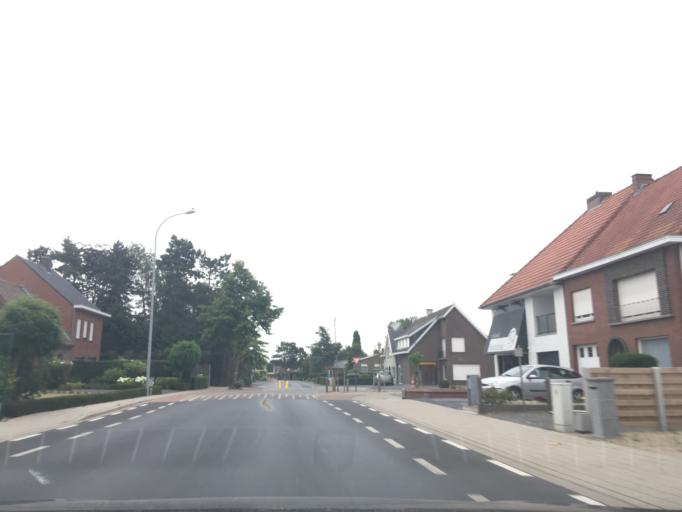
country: BE
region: Flanders
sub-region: Provincie West-Vlaanderen
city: Izegem
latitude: 50.9312
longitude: 3.2024
